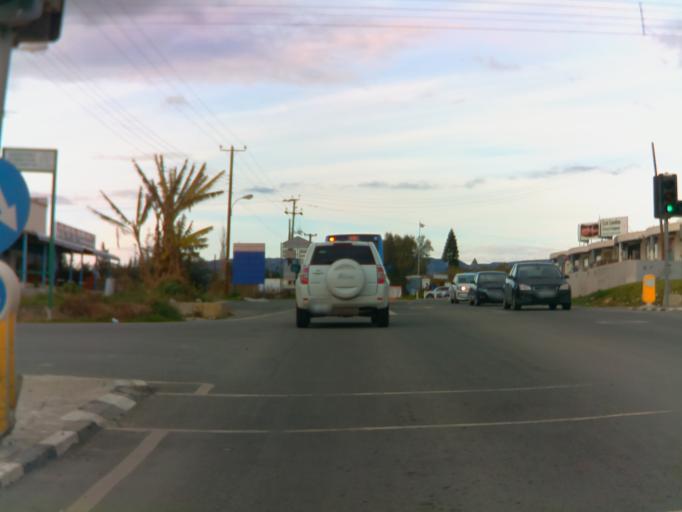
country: CY
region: Pafos
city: Kissonerga
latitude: 34.8243
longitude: 32.3924
